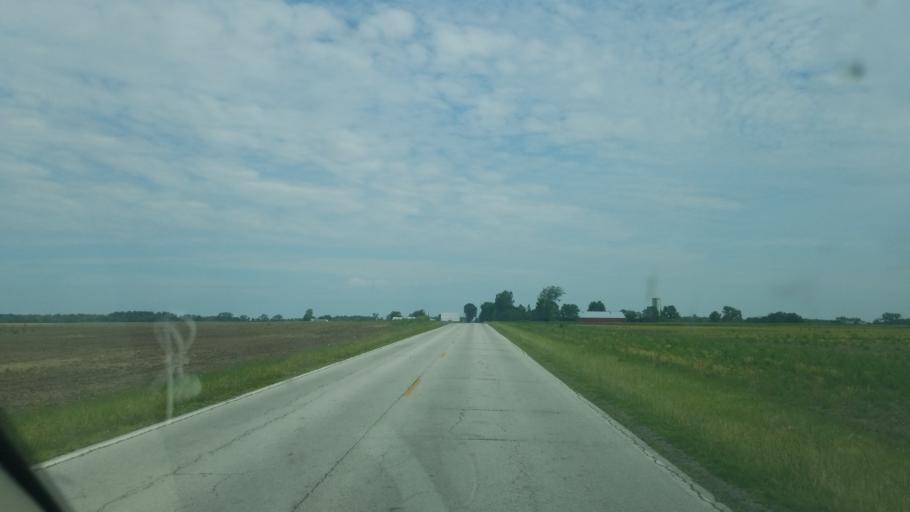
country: US
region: Ohio
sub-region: Seneca County
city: Fostoria
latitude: 41.0815
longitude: -83.4783
